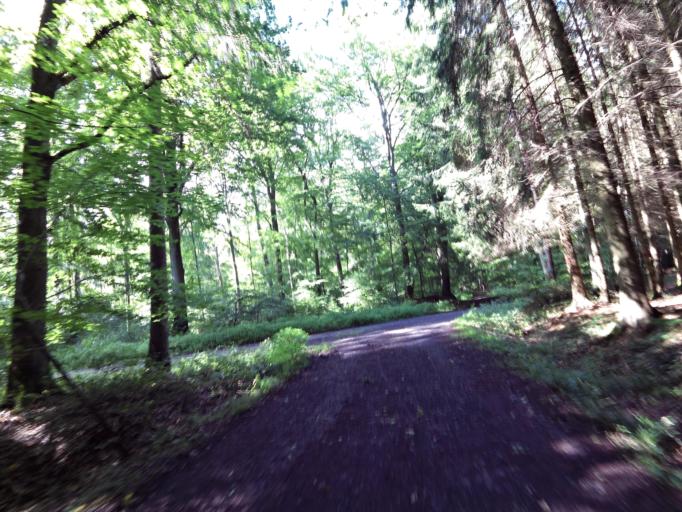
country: DE
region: Rheinland-Pfalz
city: Dernau
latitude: 50.5606
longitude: 7.0716
